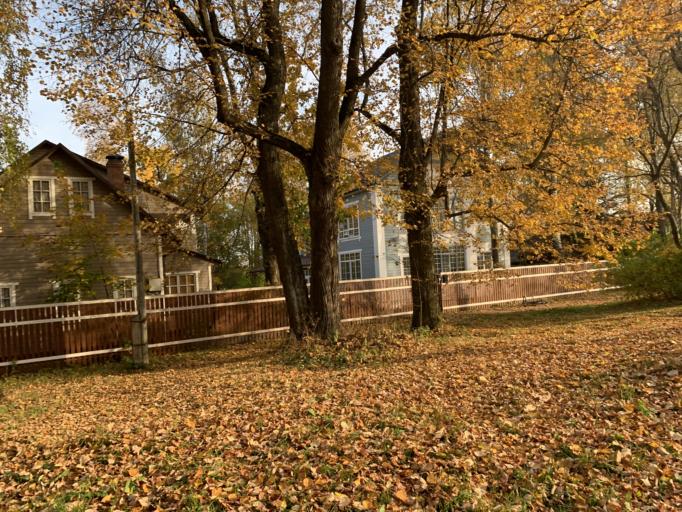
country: RU
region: Jaroslavl
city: Petrovsk
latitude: 56.9793
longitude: 39.3832
